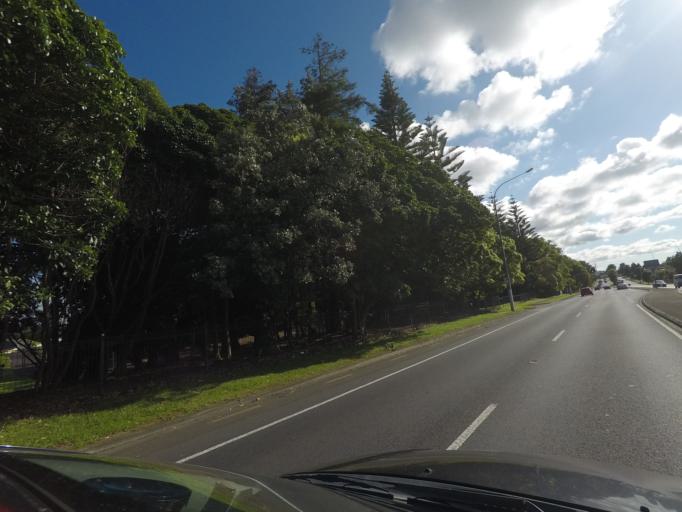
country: NZ
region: Auckland
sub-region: Auckland
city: Manukau City
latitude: -36.9848
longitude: 174.8870
